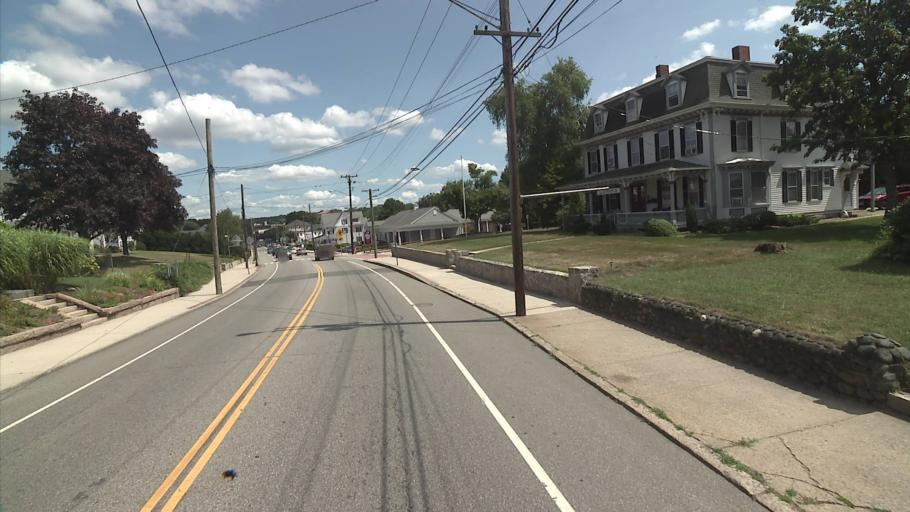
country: US
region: Connecticut
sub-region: New London County
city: Pawcatuck
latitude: 41.3762
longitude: -71.8369
